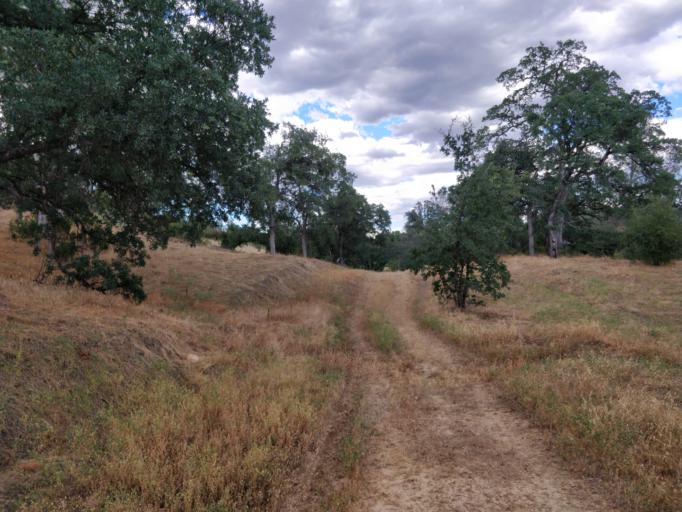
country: US
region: California
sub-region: Shasta County
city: Redding
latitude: 40.6098
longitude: -122.3849
